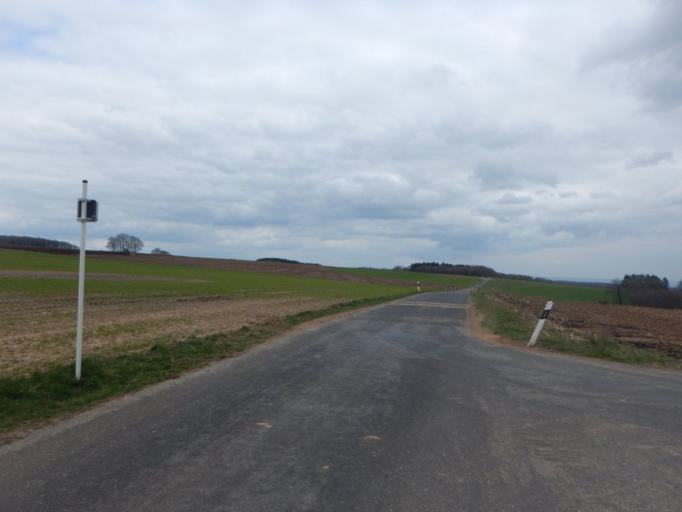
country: LU
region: Diekirch
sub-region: Canton de Redange
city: Rambrouch
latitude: 49.8033
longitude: 5.8338
